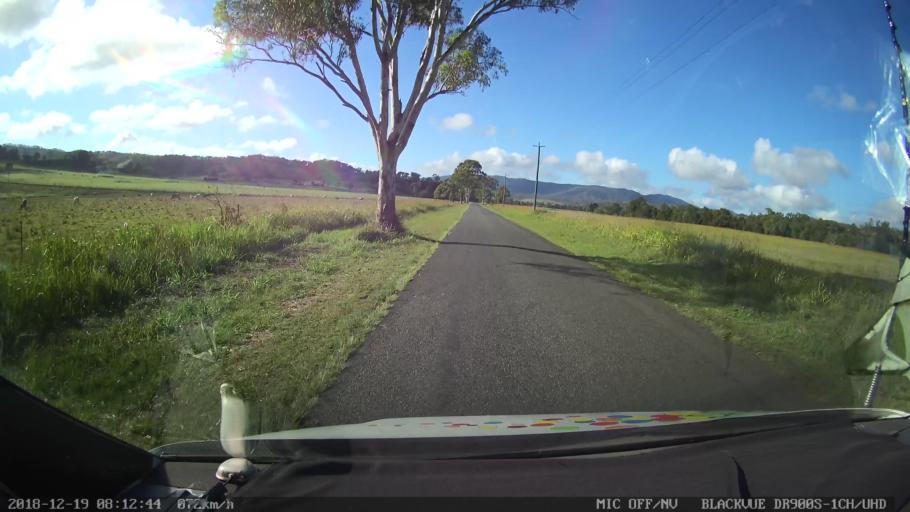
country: AU
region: Queensland
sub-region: Logan
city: Cedar Vale
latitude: -28.2305
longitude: 152.8916
